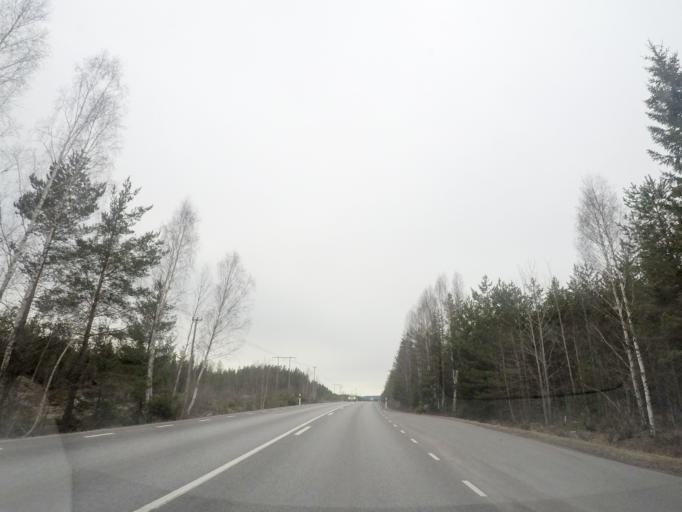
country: SE
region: Vaestmanland
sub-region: Skinnskattebergs Kommun
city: Skinnskatteberg
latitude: 59.8502
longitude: 15.6650
